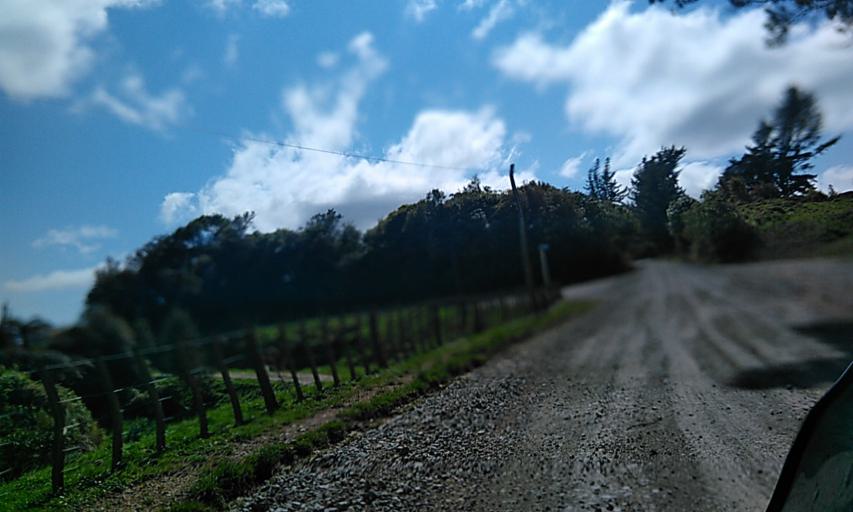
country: NZ
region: Gisborne
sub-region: Gisborne District
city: Gisborne
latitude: -38.2024
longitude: 178.0588
